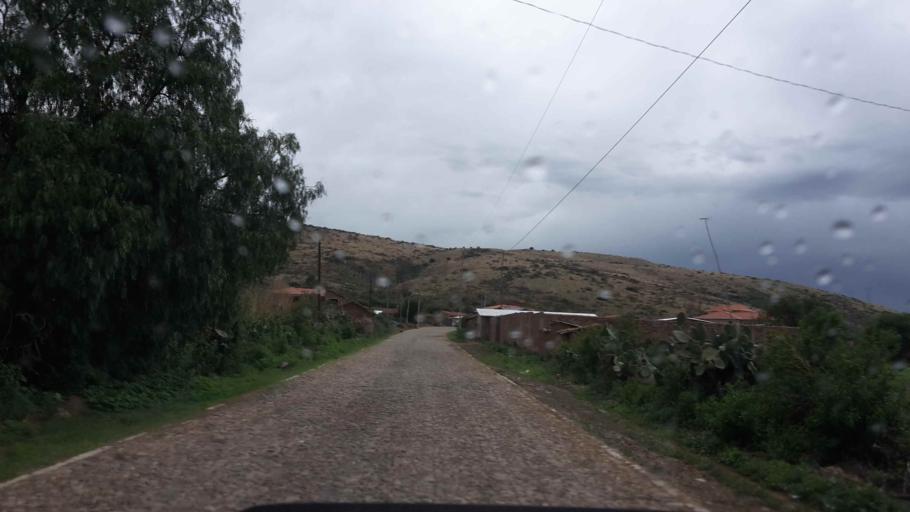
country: BO
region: Cochabamba
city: Cochabamba
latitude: -17.5483
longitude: -66.1800
